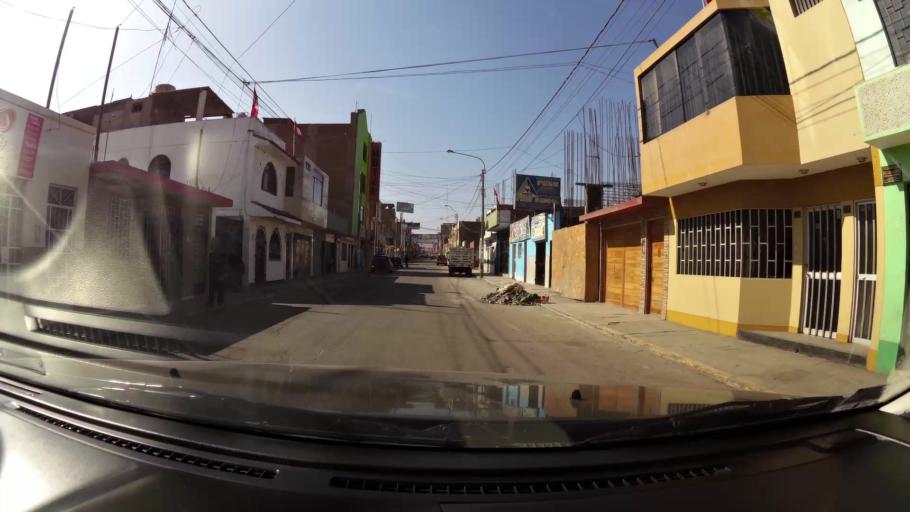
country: PE
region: Ica
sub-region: Provincia de Chincha
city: Chincha Alta
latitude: -13.4206
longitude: -76.1329
